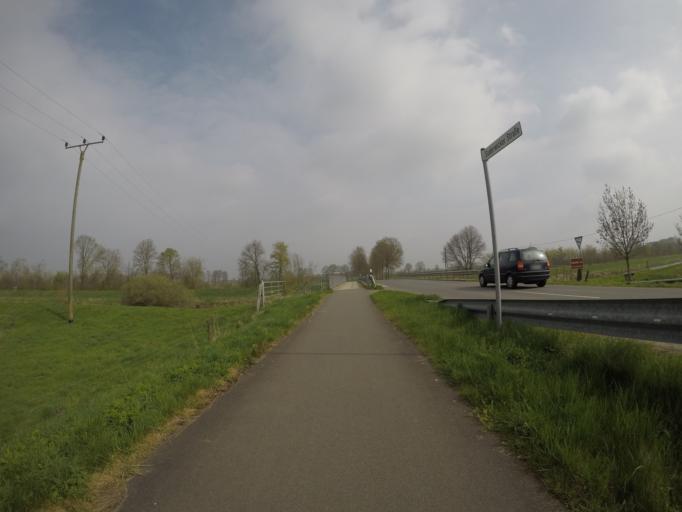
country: DE
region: North Rhine-Westphalia
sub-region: Regierungsbezirk Munster
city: Isselburg
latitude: 51.8450
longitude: 6.5019
